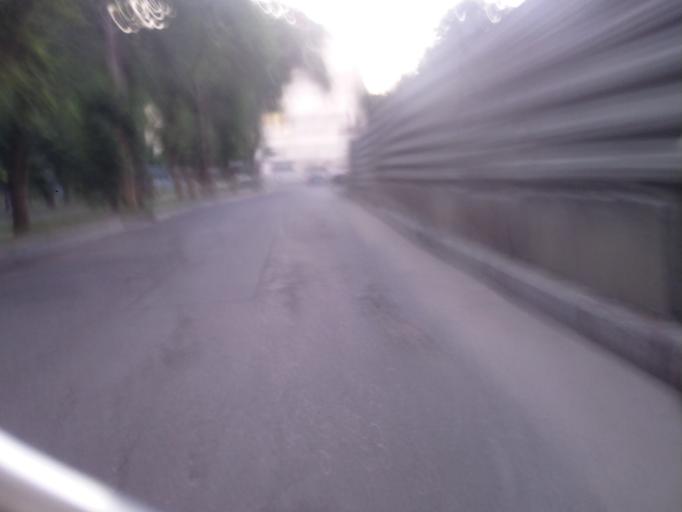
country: RU
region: Voronezj
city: Voronezh
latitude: 51.6537
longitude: 39.1774
